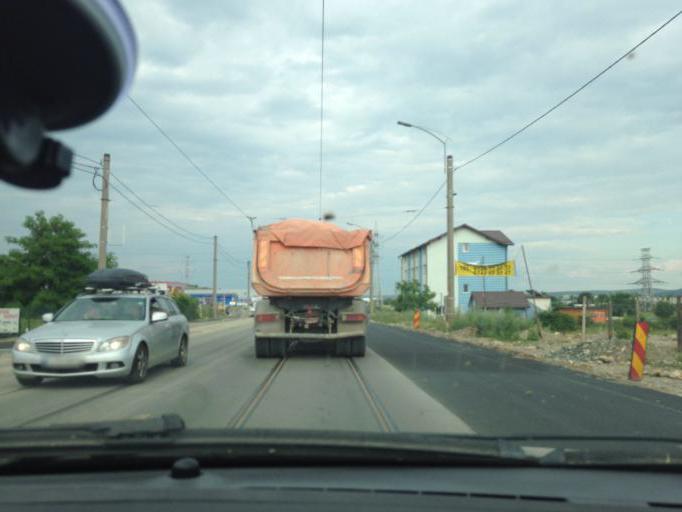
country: RO
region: Cluj
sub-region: Municipiul Cluj-Napoca
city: Cluj-Napoca
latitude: 46.7965
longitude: 23.6476
